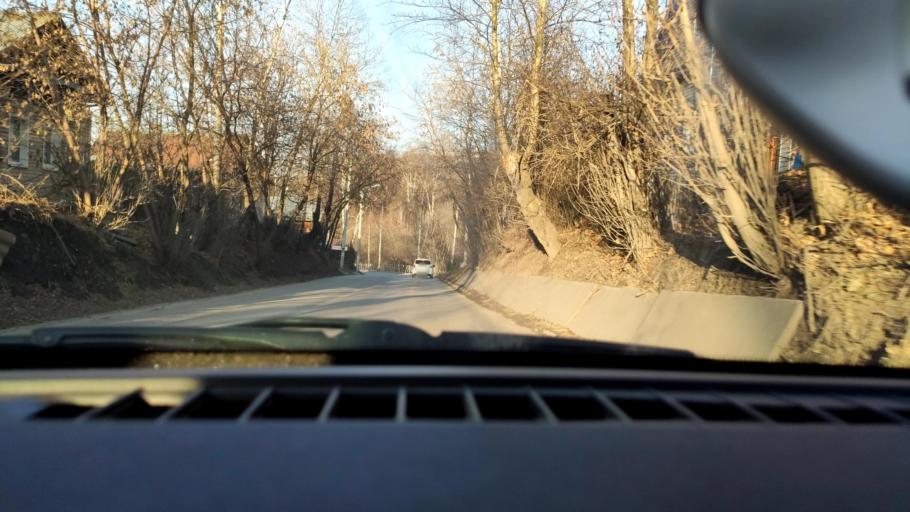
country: RU
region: Perm
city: Perm
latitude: 58.0264
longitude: 56.3144
